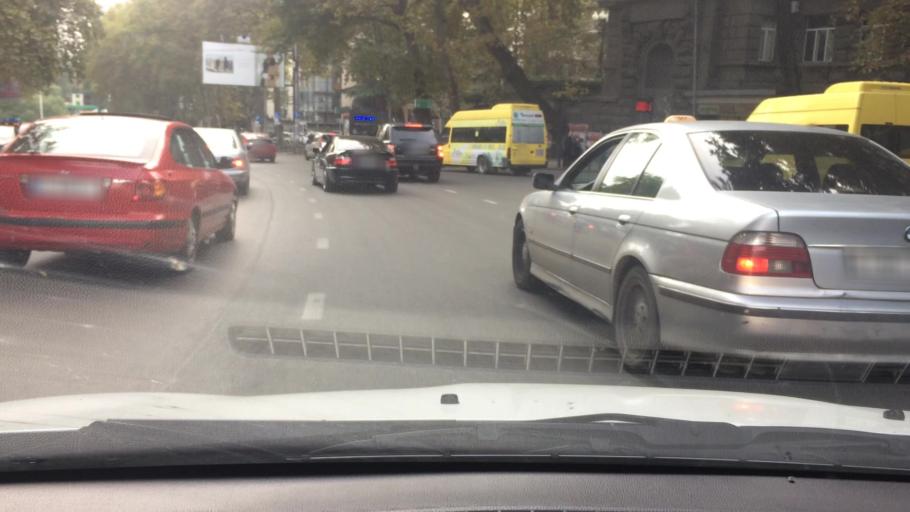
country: GE
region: T'bilisi
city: Tbilisi
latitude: 41.7164
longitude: 44.7786
